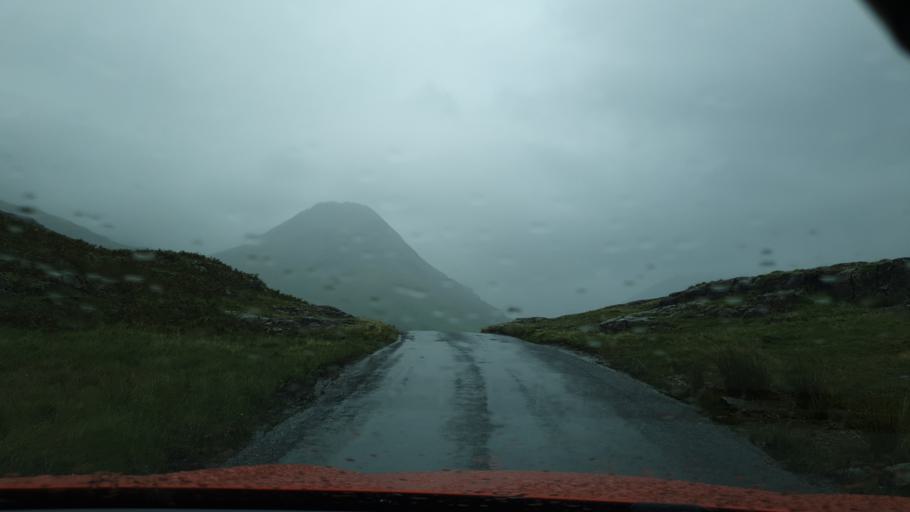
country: GB
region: England
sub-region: Cumbria
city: Seascale
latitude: 54.4427
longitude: -3.3020
